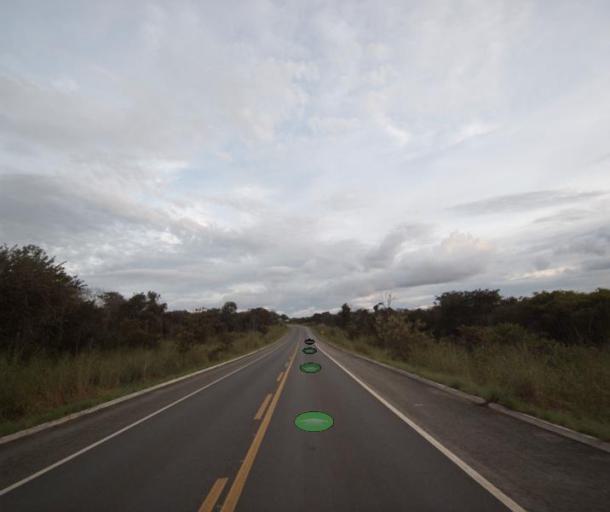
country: BR
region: Goias
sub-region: Barro Alto
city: Barro Alto
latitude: -15.1911
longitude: -48.7034
